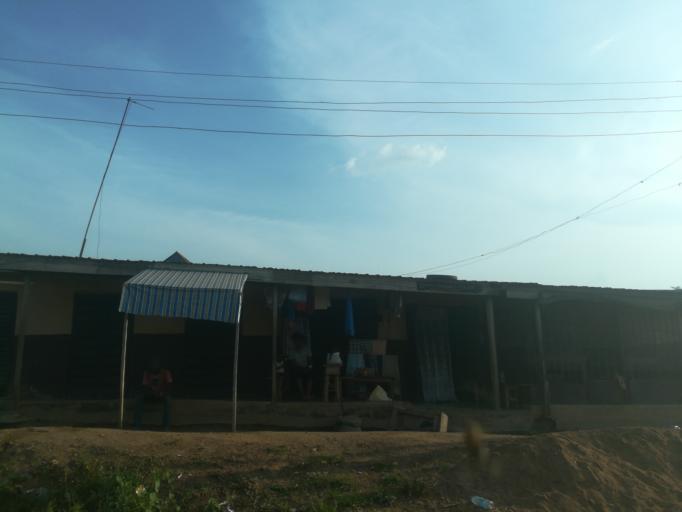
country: NG
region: Oyo
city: Moniya
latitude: 7.5521
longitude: 3.8892
